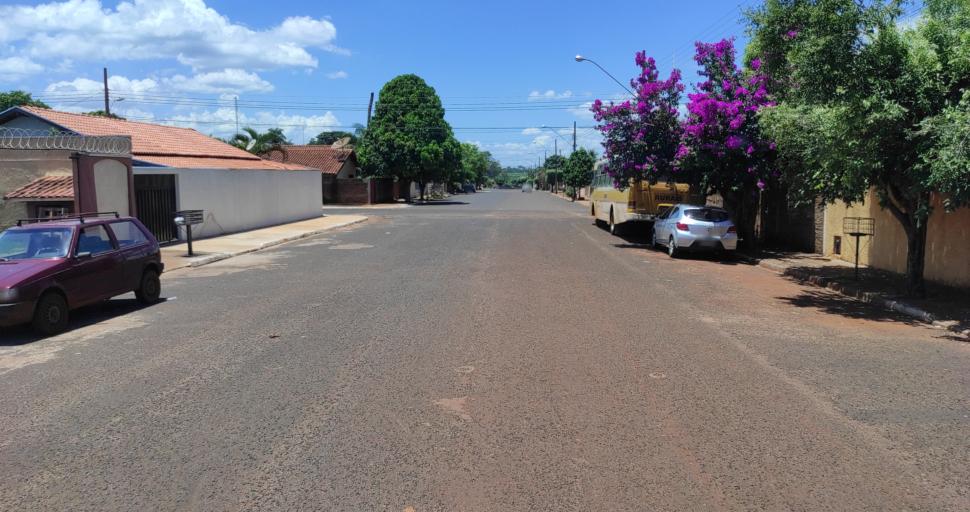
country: BR
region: Minas Gerais
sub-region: Frutal
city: Frutal
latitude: -20.1417
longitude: -48.7033
